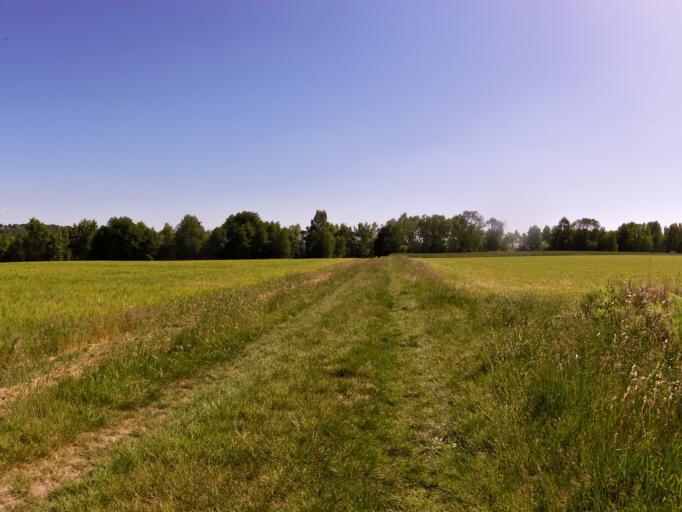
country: DE
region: Thuringia
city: Dankmarshausen
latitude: 50.9402
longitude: 10.0367
